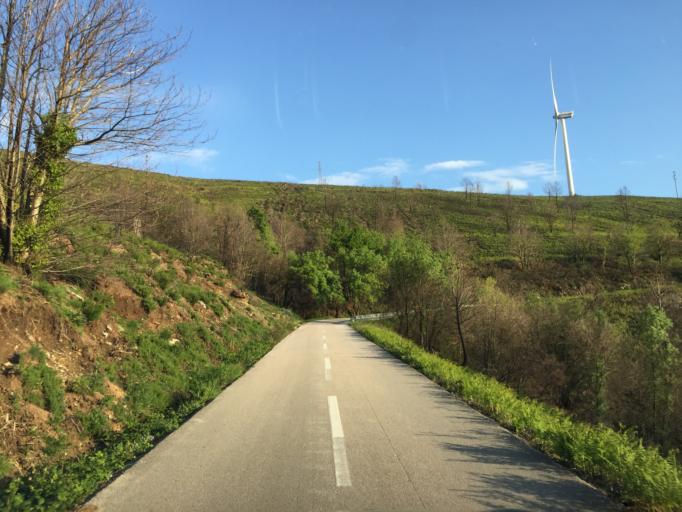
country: PT
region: Coimbra
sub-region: Pampilhosa da Serra
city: Pampilhosa da Serra
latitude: 40.1154
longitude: -8.0113
